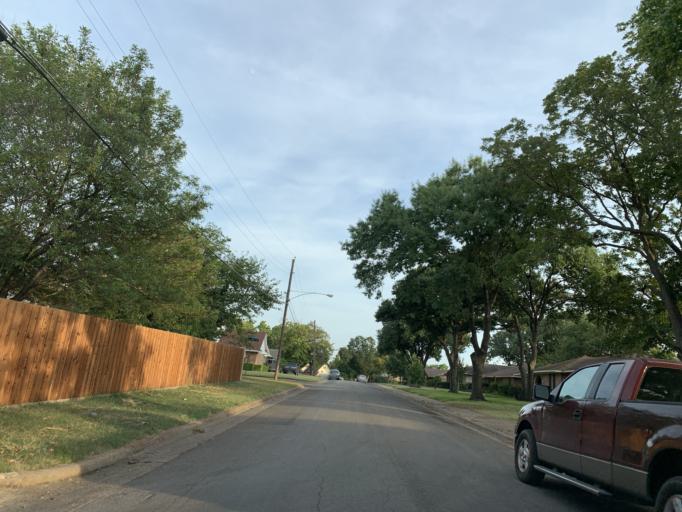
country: US
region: Texas
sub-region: Dallas County
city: Cockrell Hill
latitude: 32.6959
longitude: -96.8854
